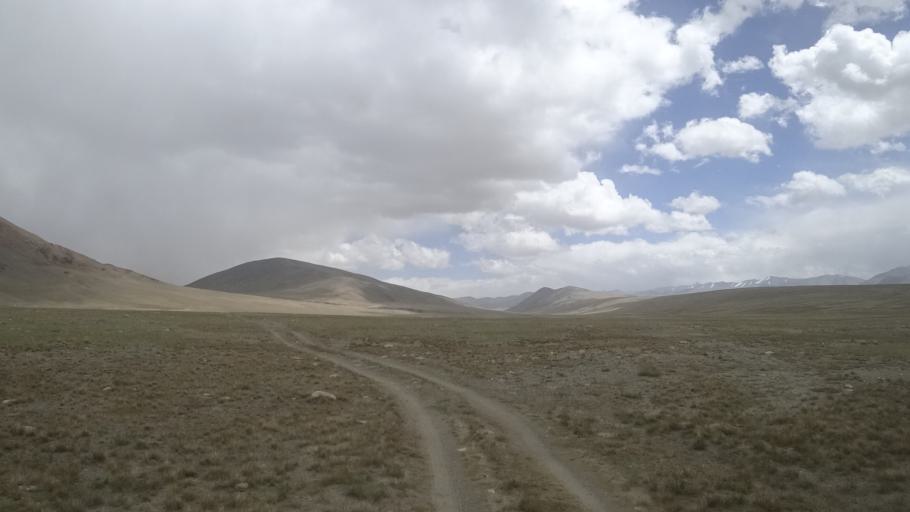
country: TJ
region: Gorno-Badakhshan
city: Murghob
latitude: 37.4890
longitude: 74.0209
